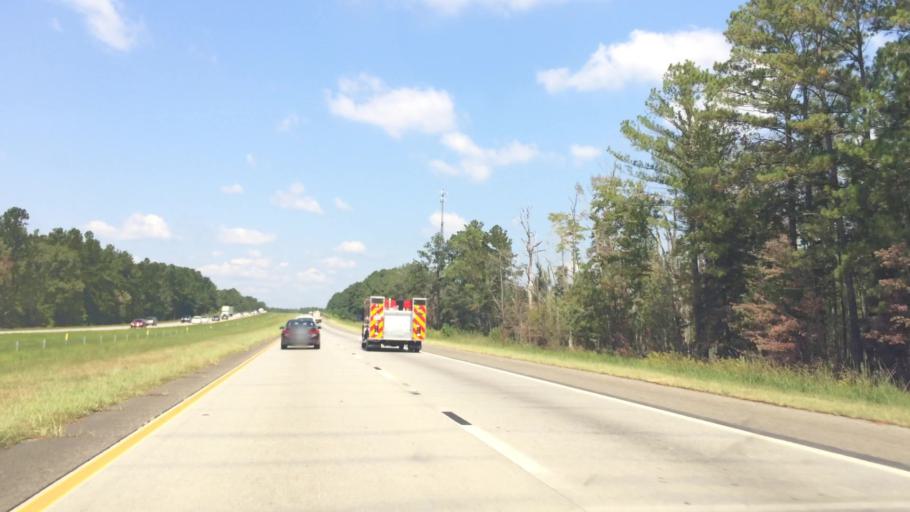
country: US
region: South Carolina
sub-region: Colleton County
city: Walterboro
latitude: 33.0298
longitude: -80.6669
